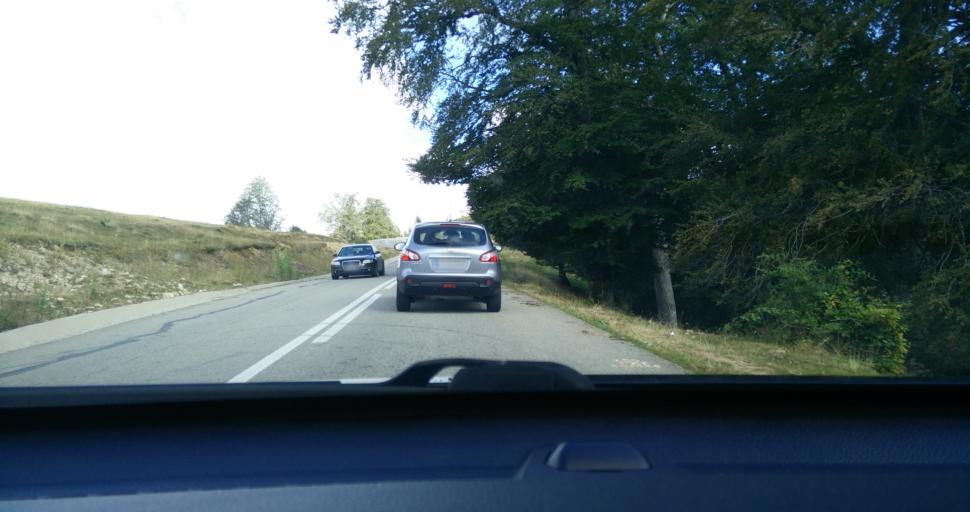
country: RO
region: Gorj
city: Novaci-Straini
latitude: 45.2305
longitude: 23.6882
